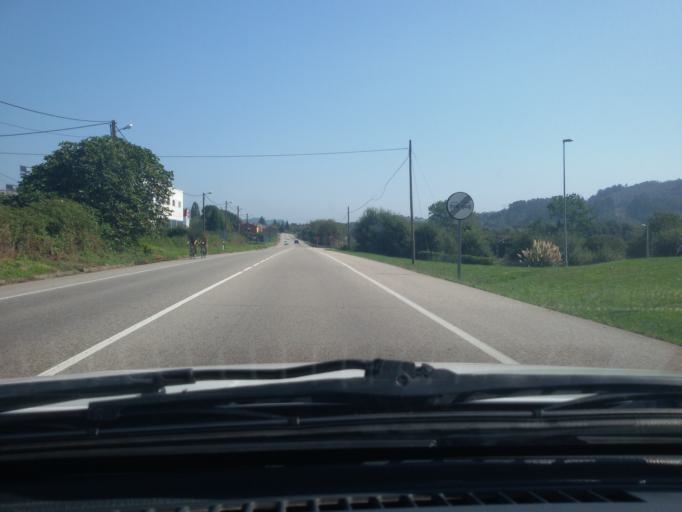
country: ES
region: Asturias
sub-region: Province of Asturias
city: Norena
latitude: 43.3871
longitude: -5.6855
